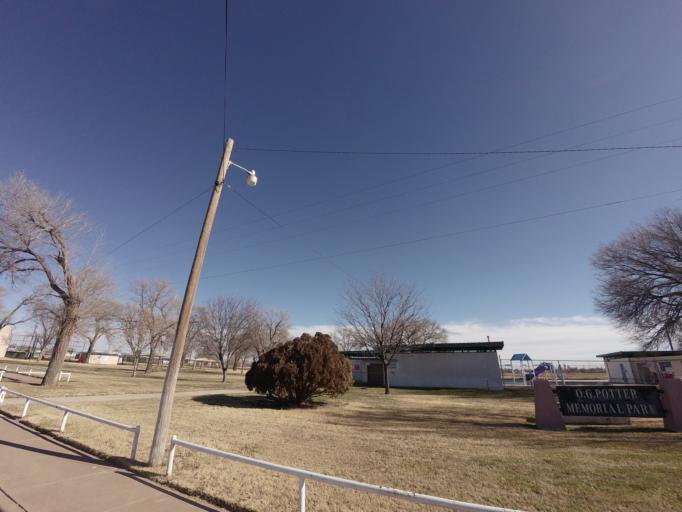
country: US
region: New Mexico
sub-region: Curry County
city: Clovis
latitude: 34.4024
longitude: -103.2305
